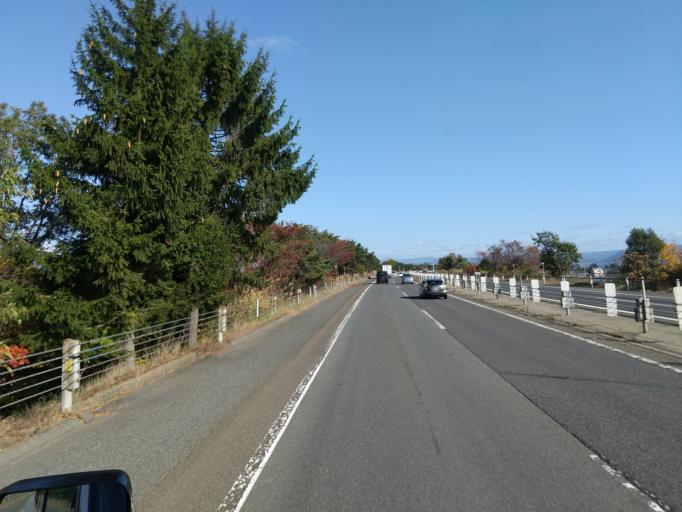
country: JP
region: Iwate
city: Morioka-shi
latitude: 39.5983
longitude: 141.1195
